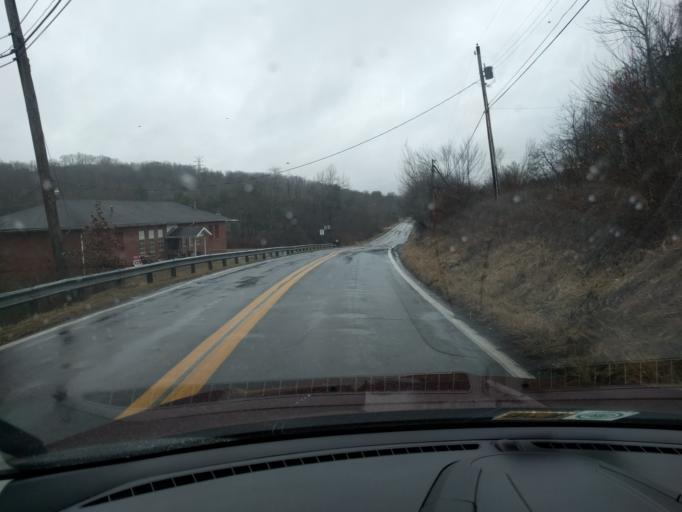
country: US
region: West Virginia
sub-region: Raleigh County
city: Beckley
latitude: 37.7901
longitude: -81.1882
